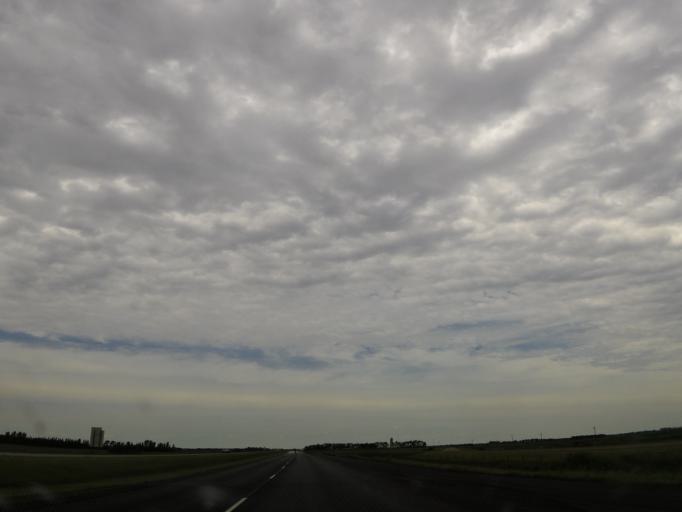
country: US
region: North Dakota
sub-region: Walsh County
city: Grafton
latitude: 48.2986
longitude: -97.1889
